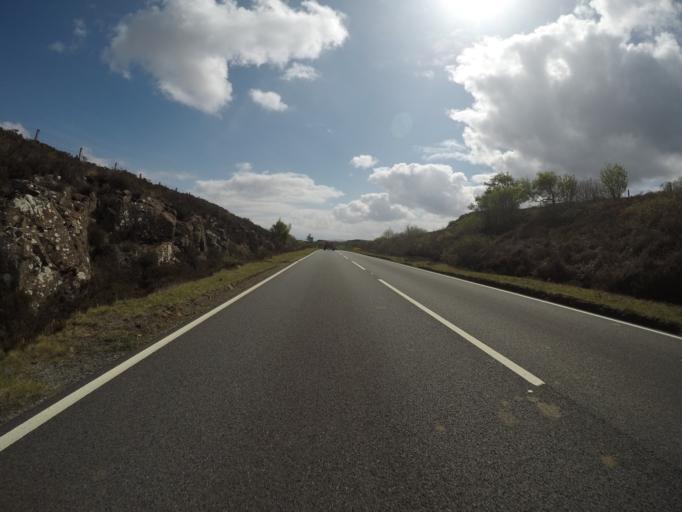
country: GB
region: Scotland
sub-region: Highland
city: Portree
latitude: 57.5137
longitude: -6.3410
